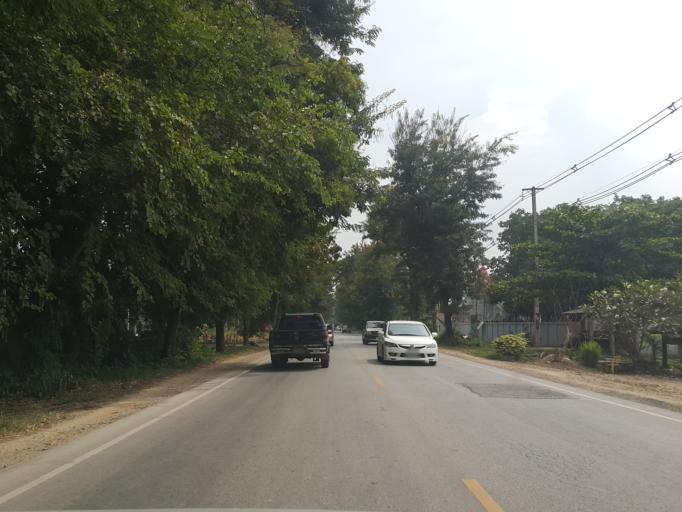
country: TH
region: Chiang Mai
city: San Sai
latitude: 18.9522
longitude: 98.9840
